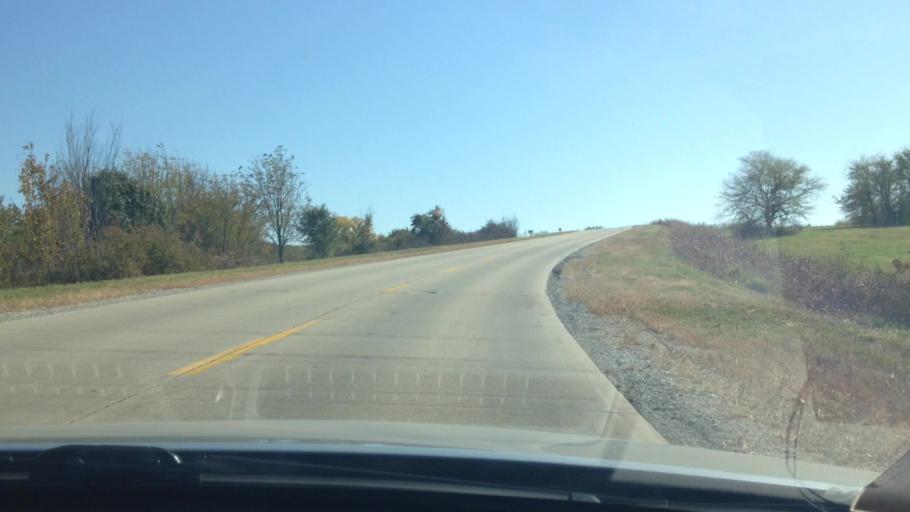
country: US
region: Missouri
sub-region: Platte County
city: Platte City
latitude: 39.3389
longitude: -94.7351
